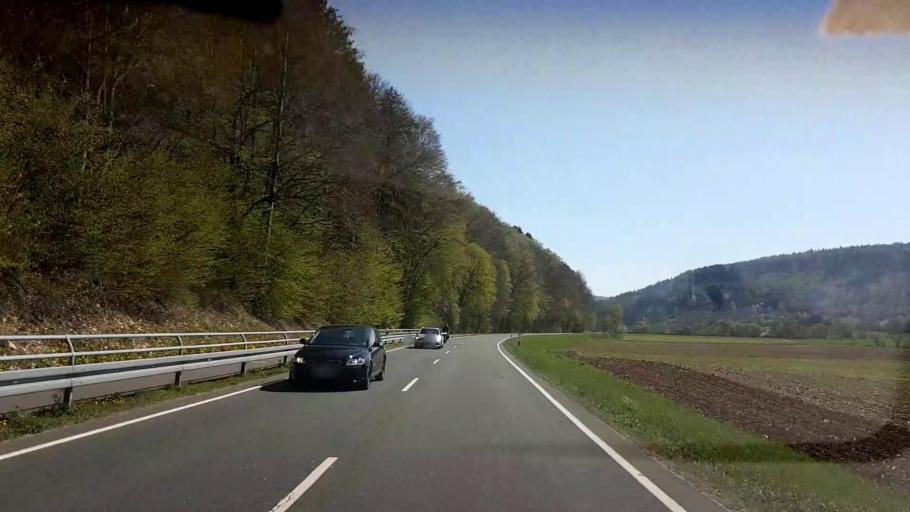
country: DE
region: Bavaria
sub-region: Upper Franconia
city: Unterleinleiter
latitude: 49.8137
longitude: 11.1946
